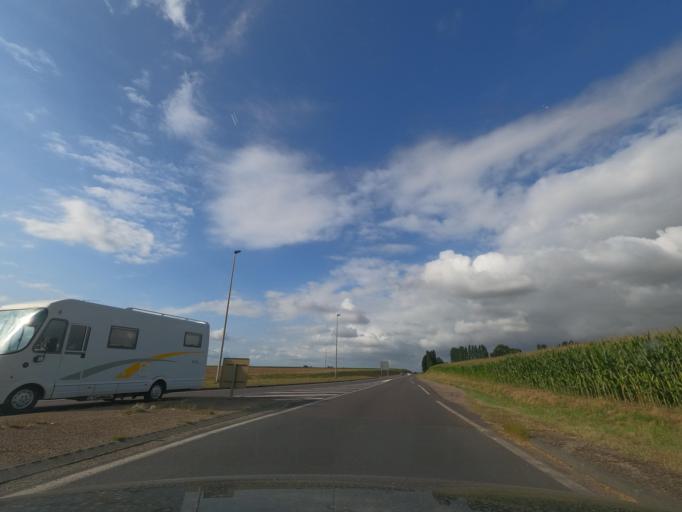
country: FR
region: Haute-Normandie
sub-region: Departement de l'Eure
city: Bernay
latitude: 49.0961
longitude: 0.5751
